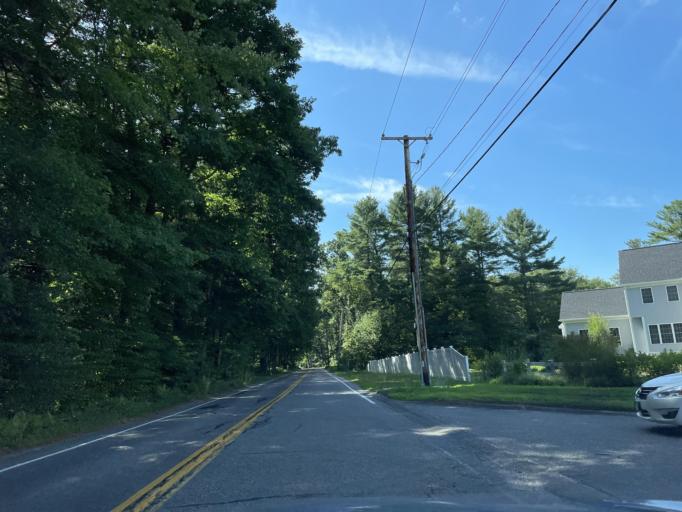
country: US
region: Massachusetts
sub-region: Worcester County
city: Mendon
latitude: 42.1187
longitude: -71.5866
